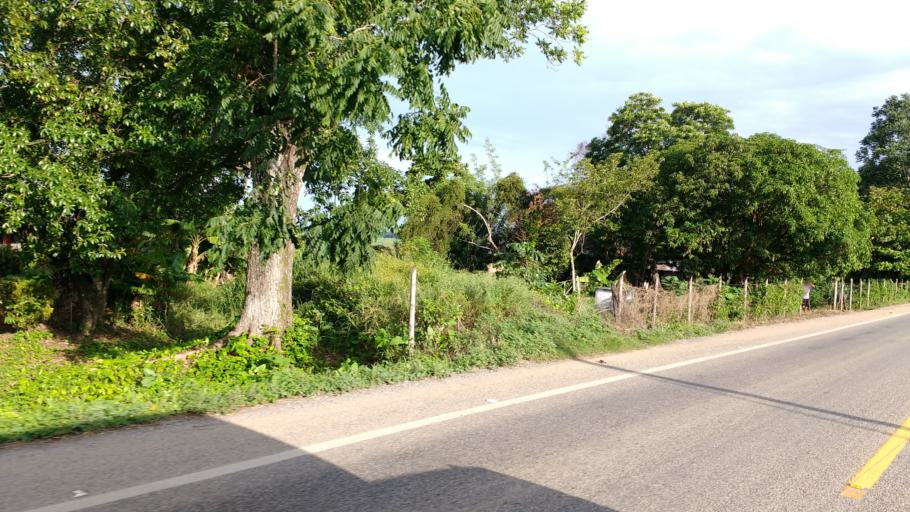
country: MX
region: Tabasco
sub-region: Teapa
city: Eureka y Belen
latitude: 17.6266
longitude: -92.9631
